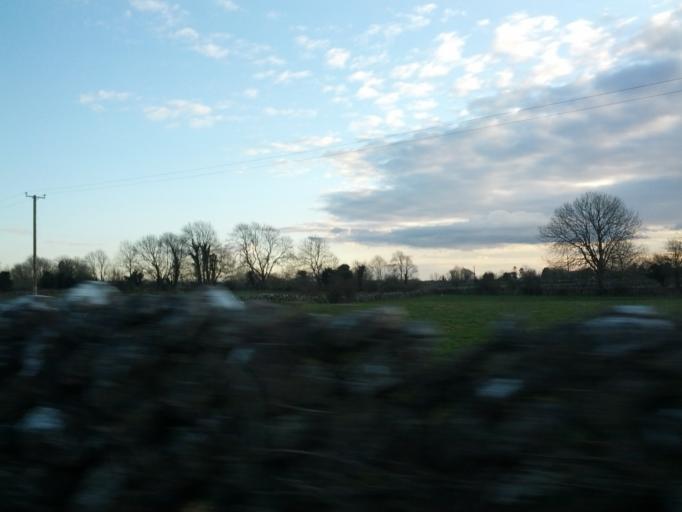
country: IE
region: Connaught
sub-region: County Galway
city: Athenry
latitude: 53.3398
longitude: -8.7123
